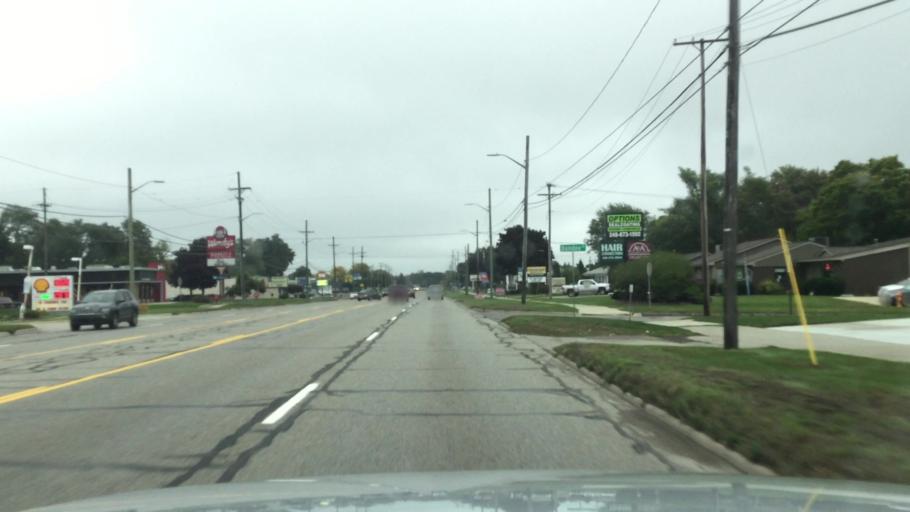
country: US
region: Michigan
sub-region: Oakland County
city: Waterford
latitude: 42.6600
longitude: -83.3999
